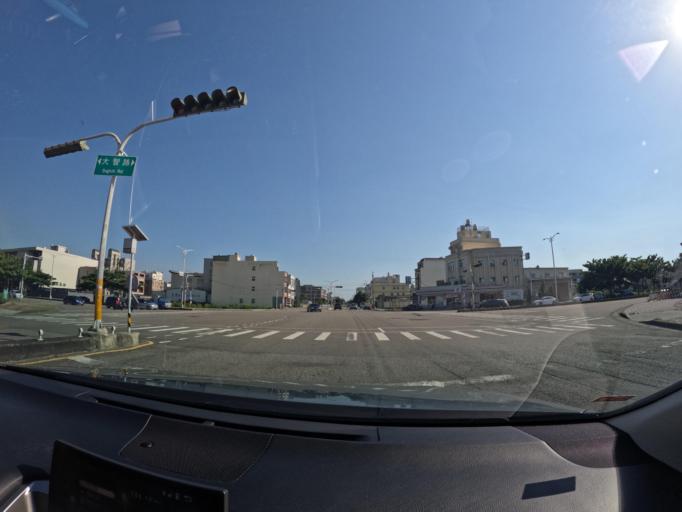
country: TW
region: Taiwan
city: Fengyuan
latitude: 24.2534
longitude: 120.5509
